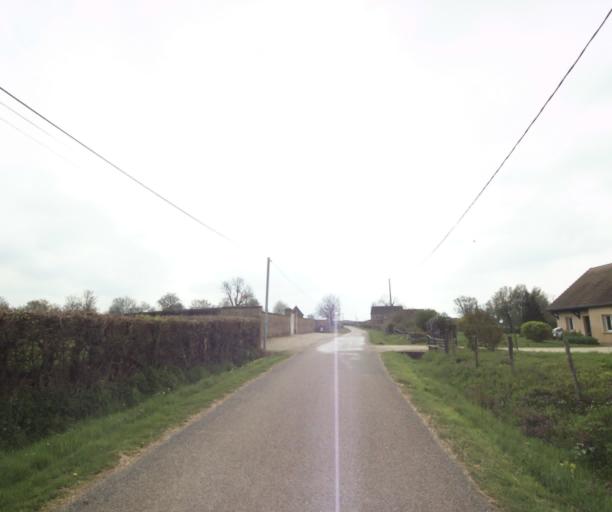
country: FR
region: Bourgogne
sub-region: Departement de Saone-et-Loire
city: Charolles
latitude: 46.3595
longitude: 4.2190
